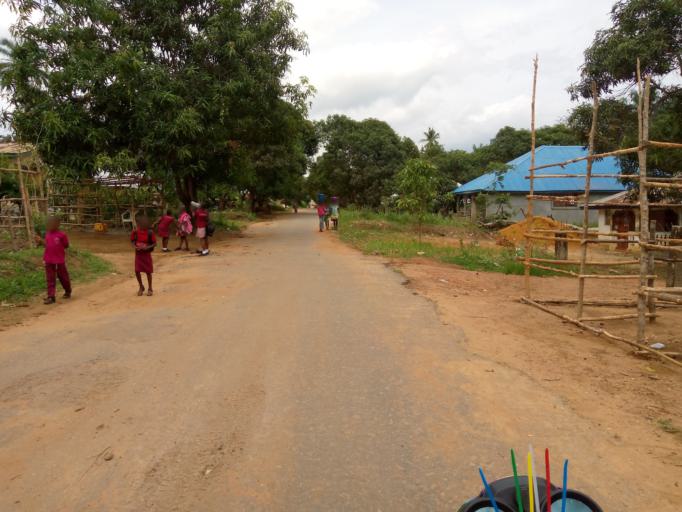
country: SL
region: Western Area
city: Waterloo
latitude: 8.3340
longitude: -13.0152
